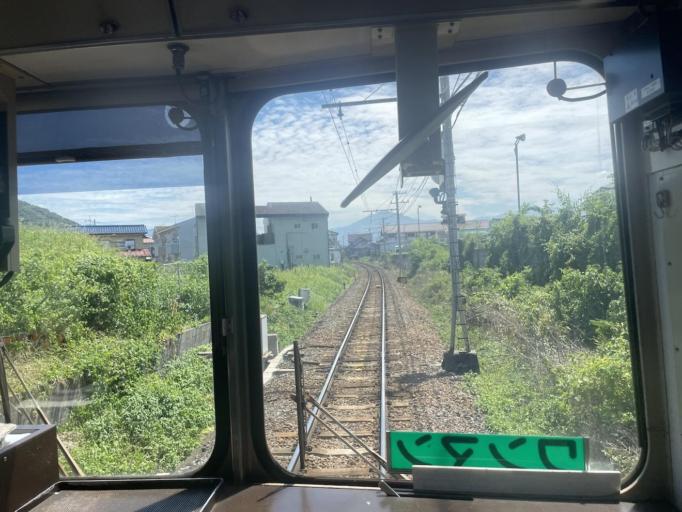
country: JP
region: Saitama
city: Chichibu
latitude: 36.0654
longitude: 139.0941
